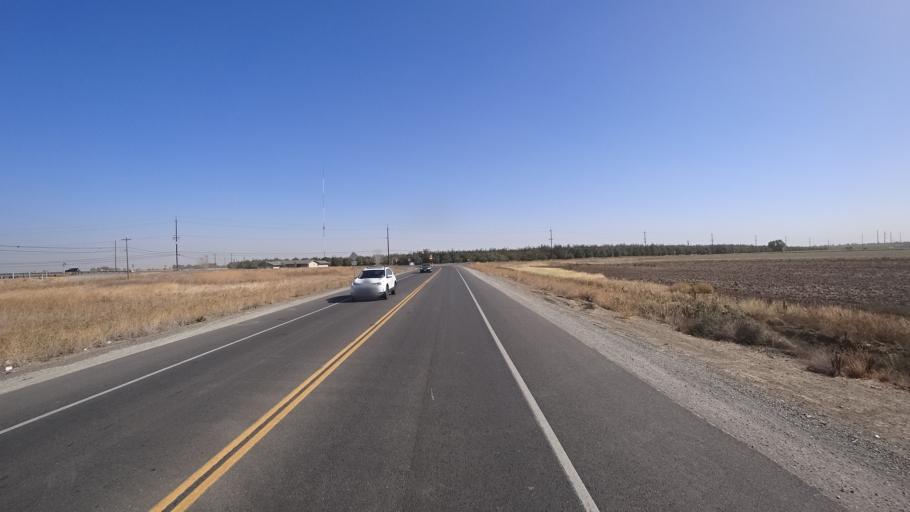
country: US
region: California
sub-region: Yolo County
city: Davis
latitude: 38.5894
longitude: -121.7319
